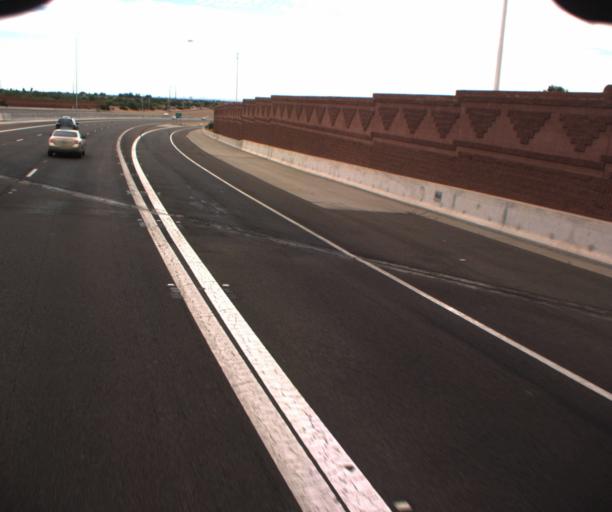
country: US
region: Arizona
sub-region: Pinal County
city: Apache Junction
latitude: 33.4282
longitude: -111.6366
